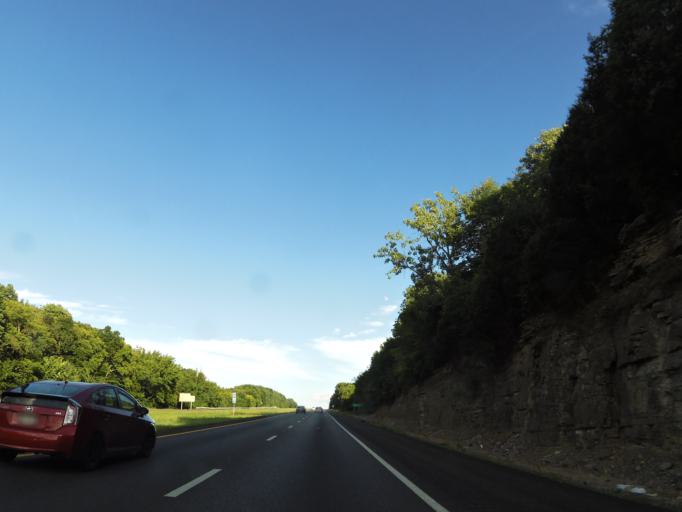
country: US
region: Tennessee
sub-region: Wilson County
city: Watertown
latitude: 36.1854
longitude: -86.1599
